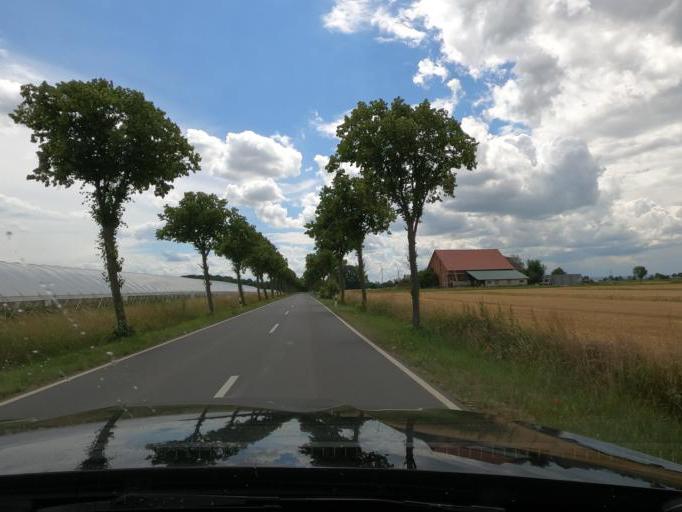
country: DE
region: Lower Saxony
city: Algermissen
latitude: 52.2793
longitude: 10.0136
